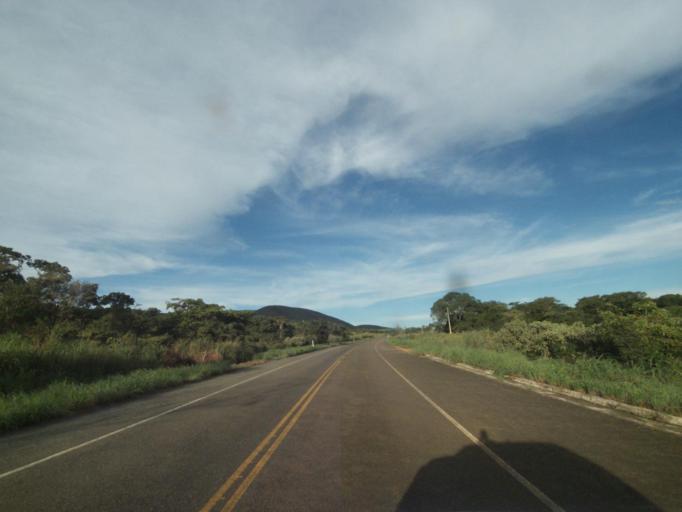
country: BR
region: Goias
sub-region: Jaragua
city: Jaragua
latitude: -15.8399
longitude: -49.3236
